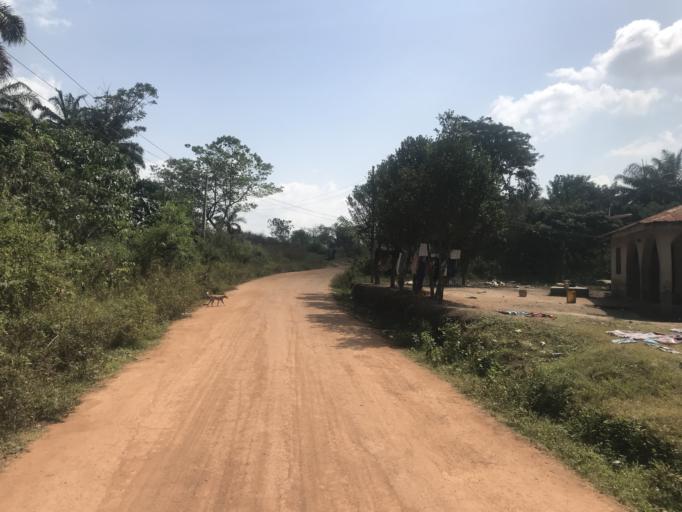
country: NG
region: Osun
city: Iragbiji
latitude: 7.8901
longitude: 4.7017
